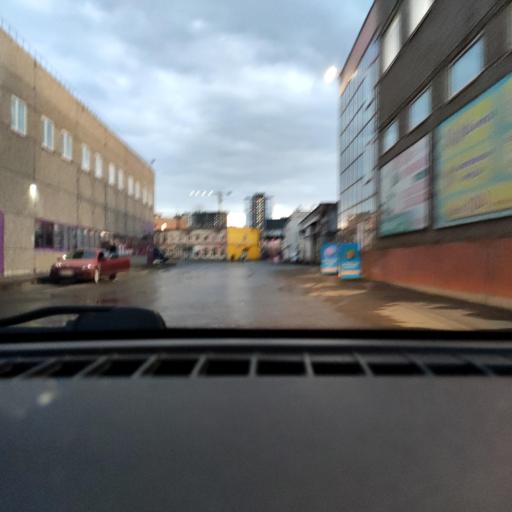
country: RU
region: Perm
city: Kondratovo
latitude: 58.0052
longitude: 56.1553
